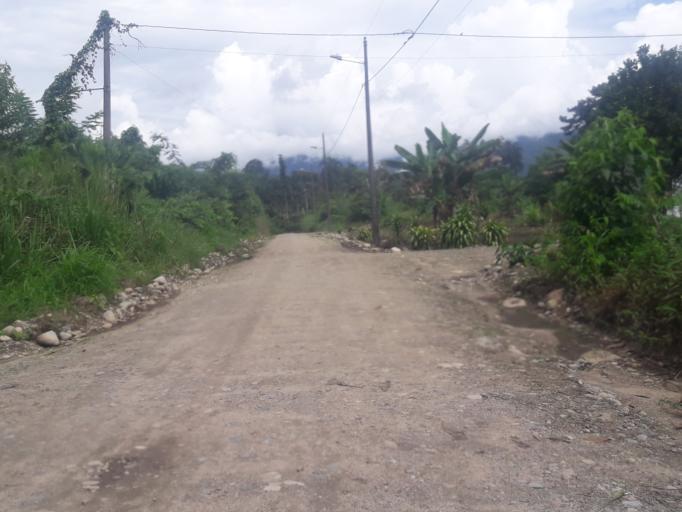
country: EC
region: Napo
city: Tena
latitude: -0.9753
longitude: -77.8463
